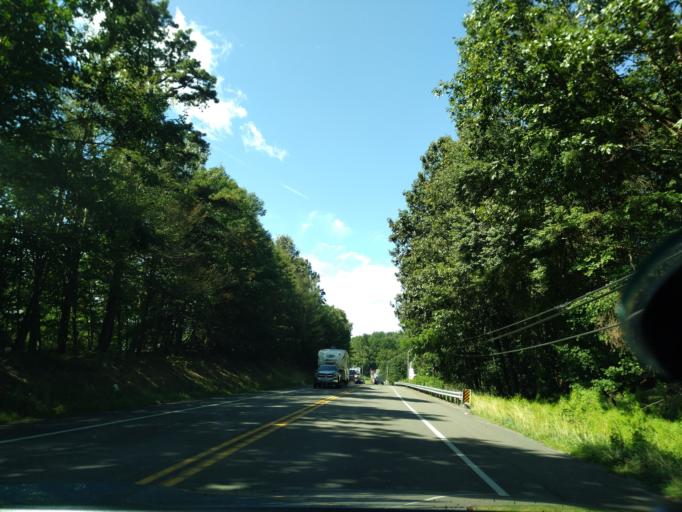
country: US
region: Pennsylvania
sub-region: Pike County
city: Saw Creek
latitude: 41.0751
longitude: -75.0334
